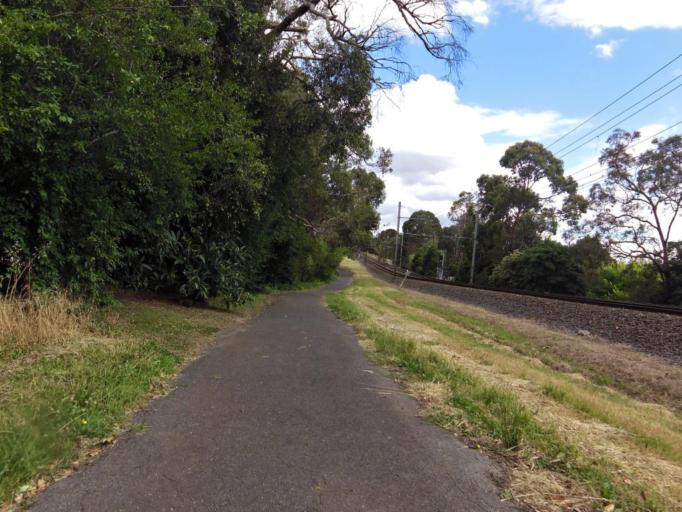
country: AU
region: Victoria
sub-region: Maroondah
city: Ringwood East
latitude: -37.8217
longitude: 145.2410
